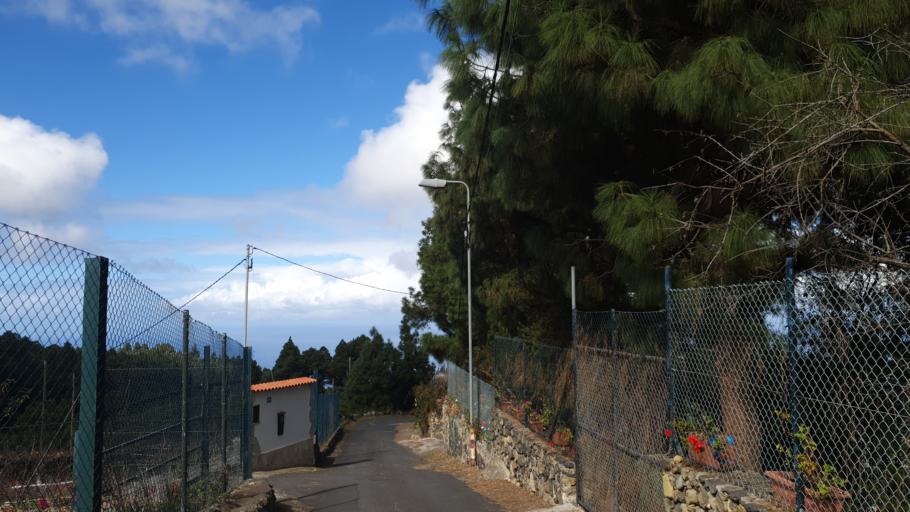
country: ES
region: Canary Islands
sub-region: Provincia de Santa Cruz de Tenerife
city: La Guancha
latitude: 28.3524
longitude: -16.6852
